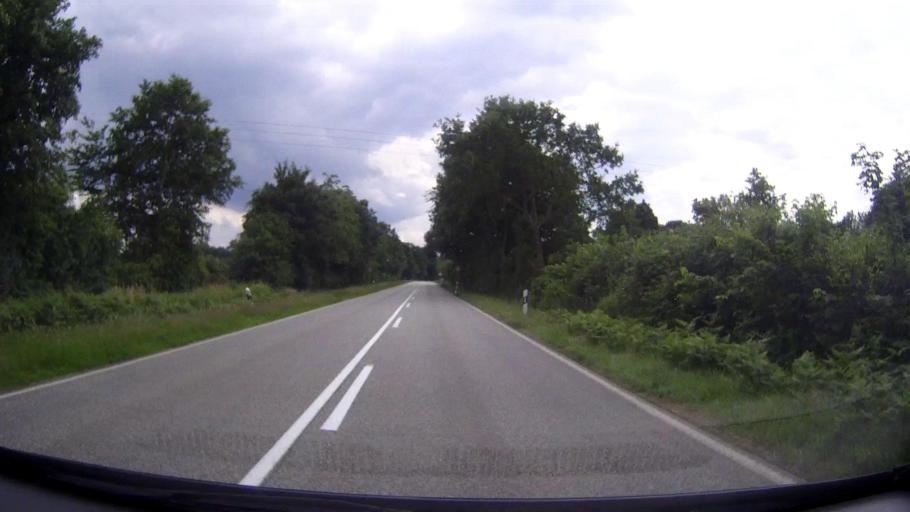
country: DE
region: Schleswig-Holstein
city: Warringholz
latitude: 54.0838
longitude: 9.4647
